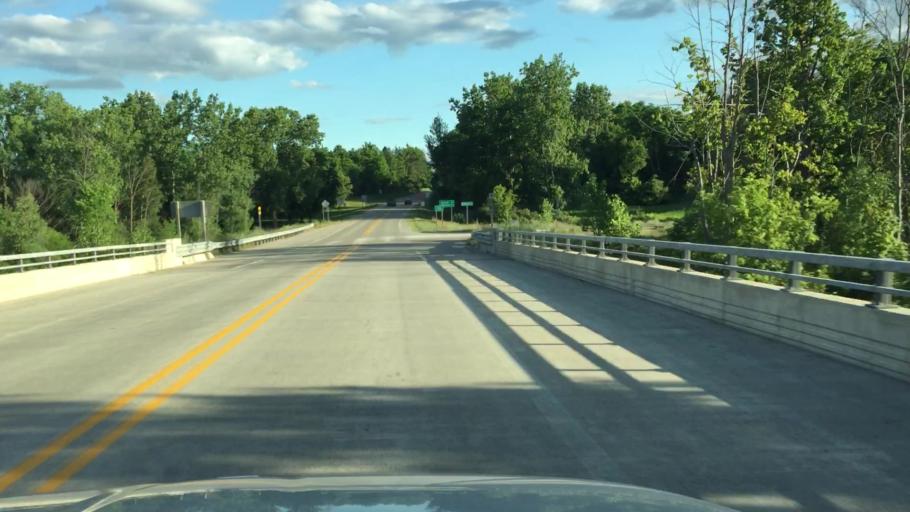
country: US
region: Michigan
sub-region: Saint Clair County
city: Yale
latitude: 43.0730
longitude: -82.7657
